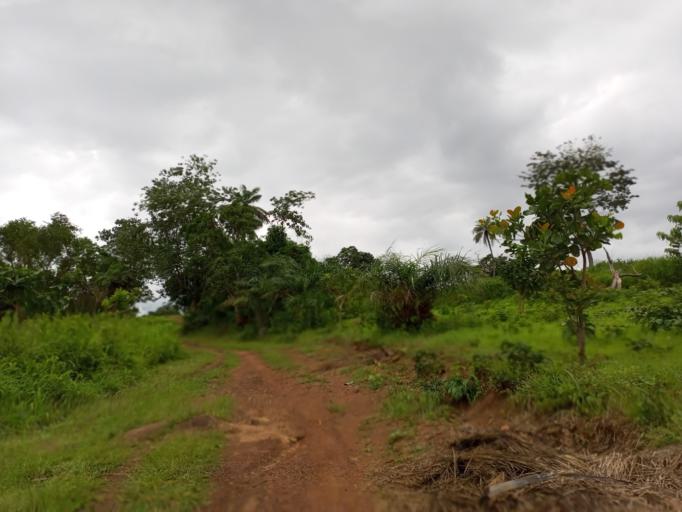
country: SL
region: Northern Province
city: Kamakwie
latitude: 9.5021
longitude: -12.2706
